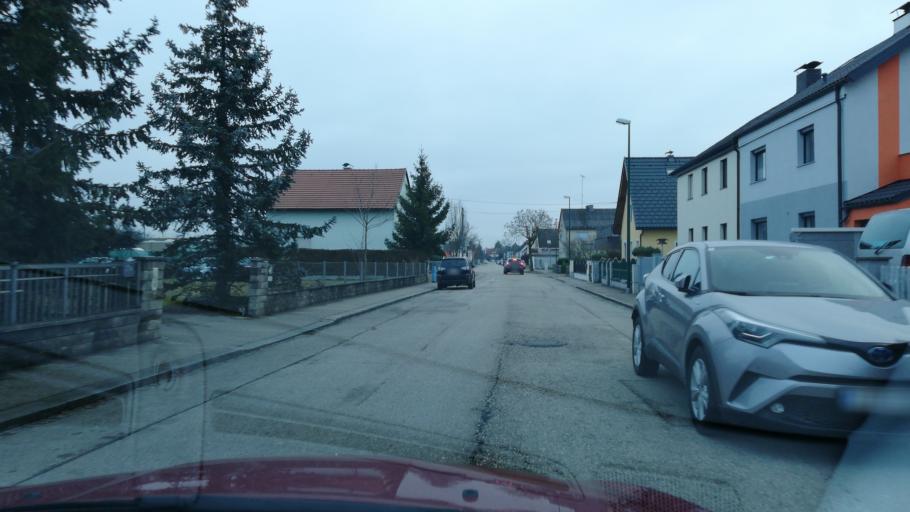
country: AT
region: Upper Austria
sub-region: Wels Stadt
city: Wels
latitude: 48.1739
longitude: 14.0491
